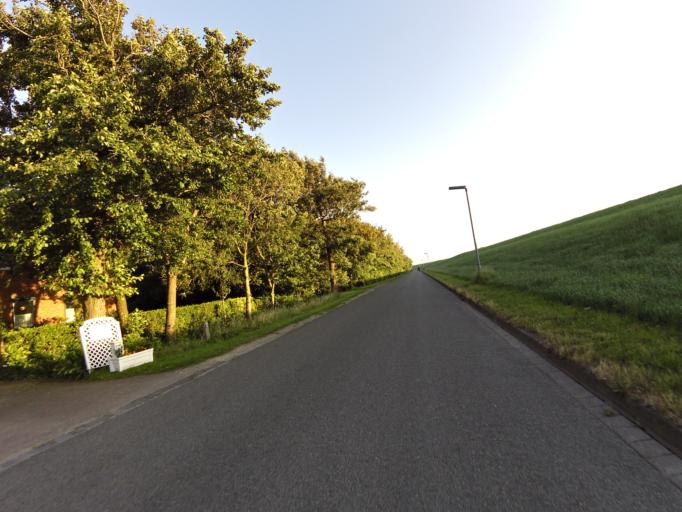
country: DE
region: Lower Saxony
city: Cappel
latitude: 53.7575
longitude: 8.5341
